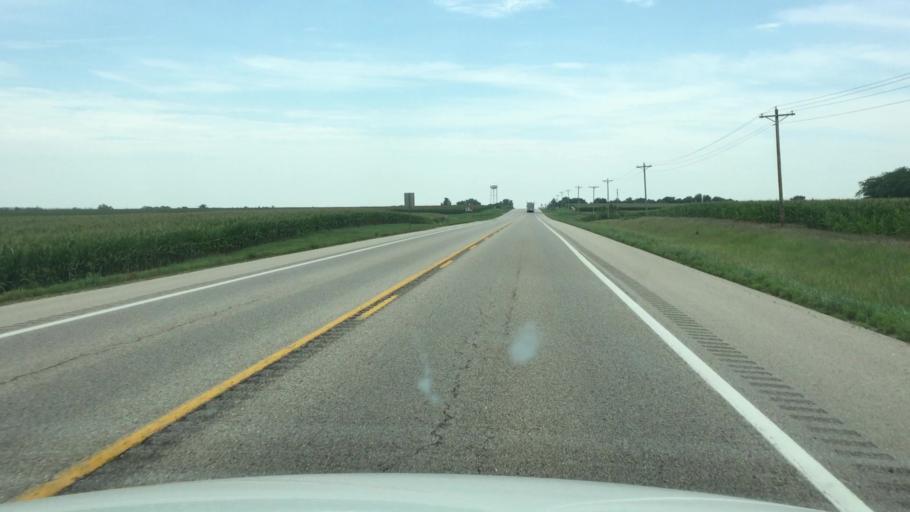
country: US
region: Kansas
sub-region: Nemaha County
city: Sabetha
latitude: 39.7140
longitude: -95.7300
